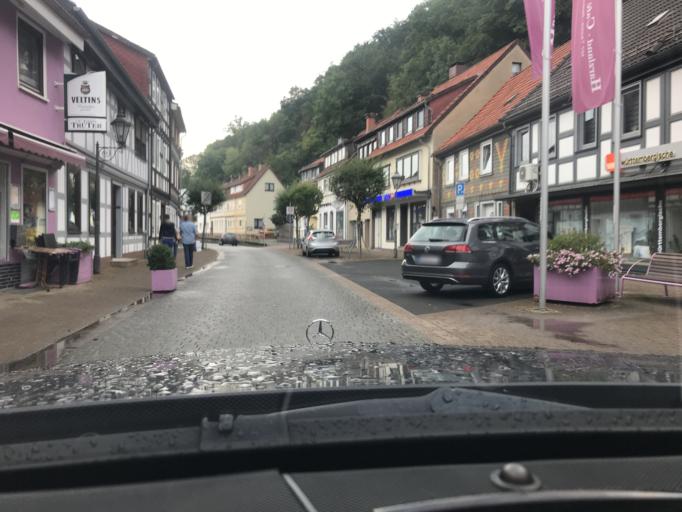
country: DE
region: Lower Saxony
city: Bad Lauterberg im Harz
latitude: 51.6286
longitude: 10.4645
